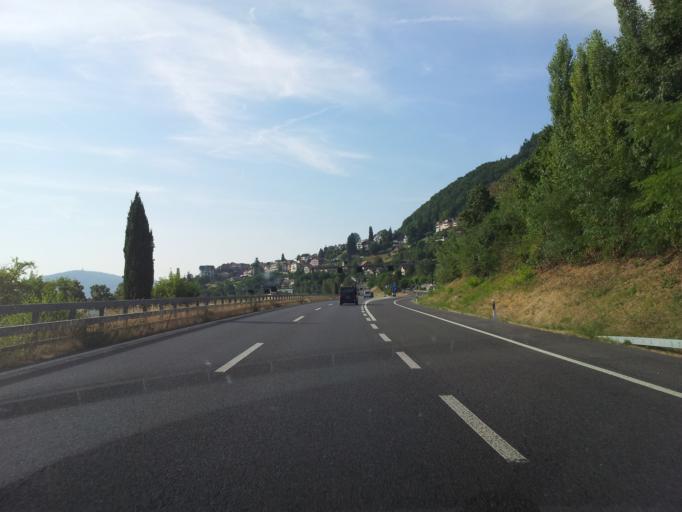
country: CH
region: Vaud
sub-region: Riviera-Pays-d'Enhaut District
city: Montreux
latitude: 46.4368
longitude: 6.9174
